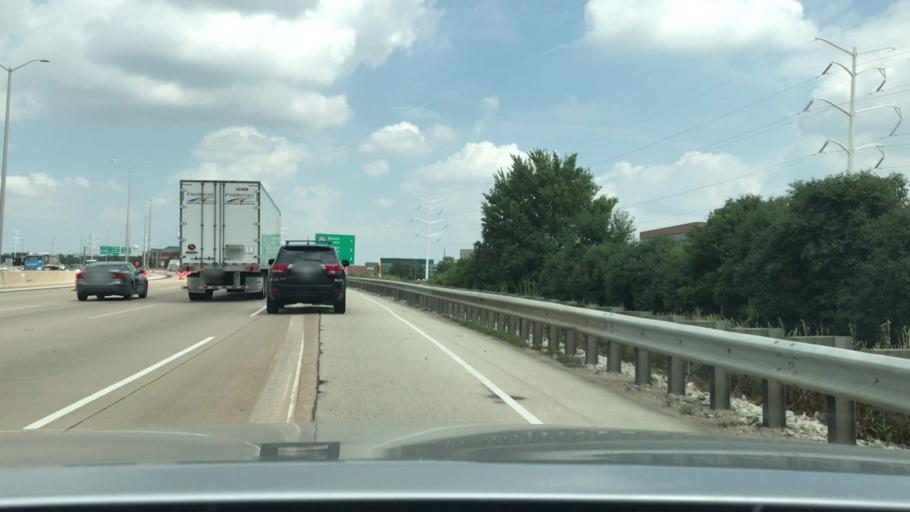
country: US
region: Illinois
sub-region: DuPage County
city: Oakbrook Terrace
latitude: 41.8446
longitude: -87.9493
